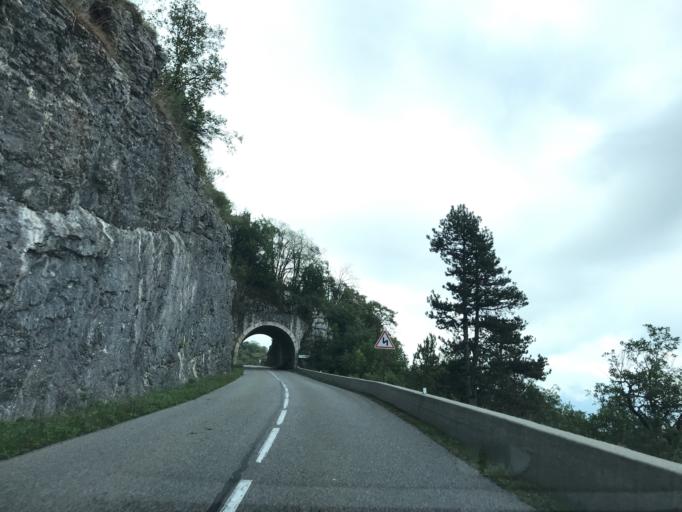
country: FR
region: Rhone-Alpes
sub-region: Departement de la Haute-Savoie
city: Talloires
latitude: 45.8434
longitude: 6.2212
